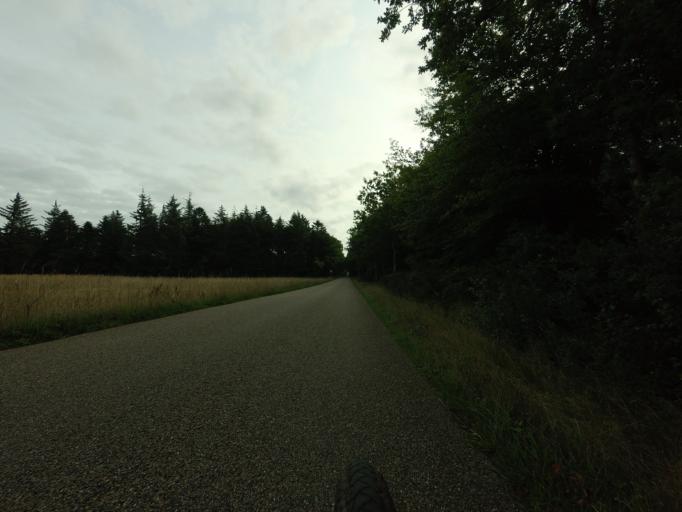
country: DK
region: North Denmark
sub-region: Hjorring Kommune
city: Hirtshals
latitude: 57.5790
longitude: 10.0846
